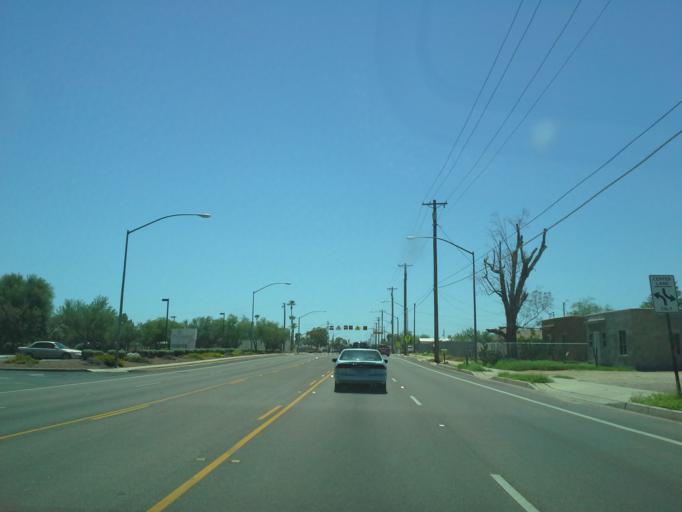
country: US
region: Arizona
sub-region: Pima County
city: Flowing Wells
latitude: 32.2753
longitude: -110.9720
